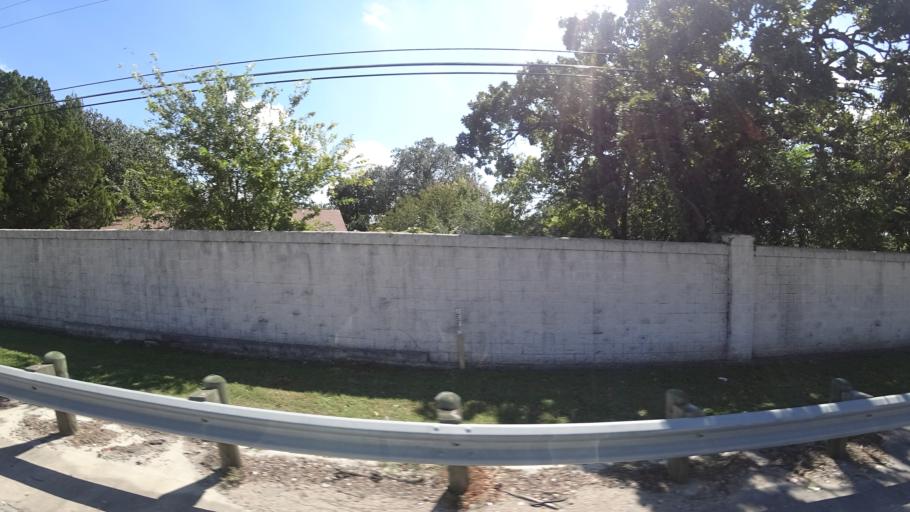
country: US
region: Texas
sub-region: Williamson County
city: Anderson Mill
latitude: 30.4631
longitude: -97.8128
